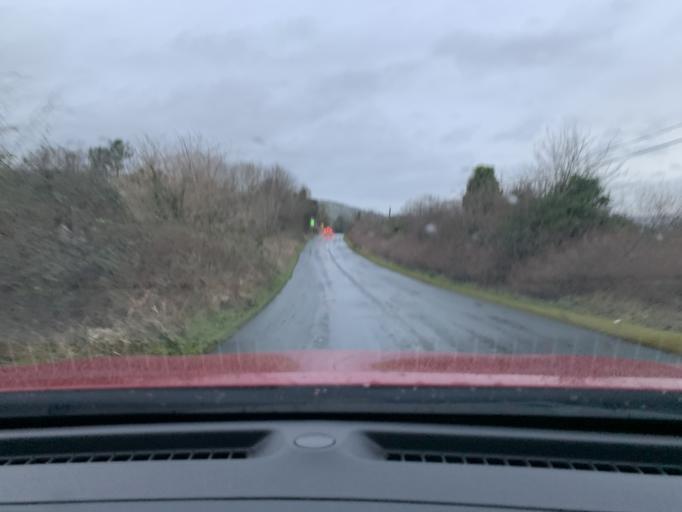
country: IE
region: Connaught
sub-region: Roscommon
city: Boyle
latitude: 54.0227
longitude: -8.3282
